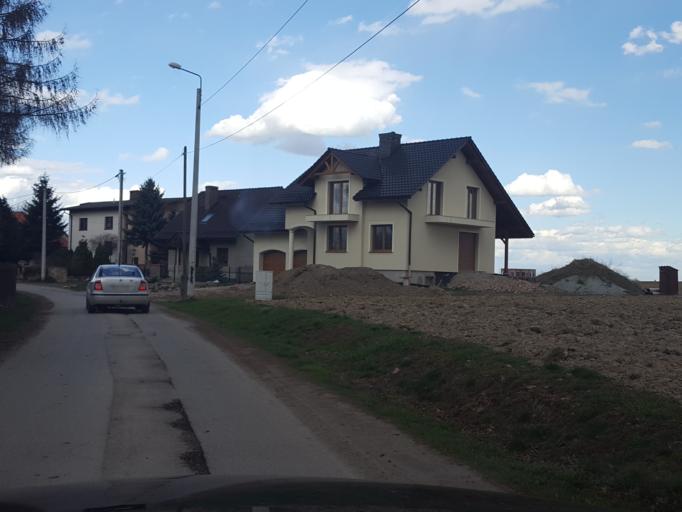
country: PL
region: Silesian Voivodeship
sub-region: Powiat bielski
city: Zabrzeg
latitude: 49.9507
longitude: 18.9070
